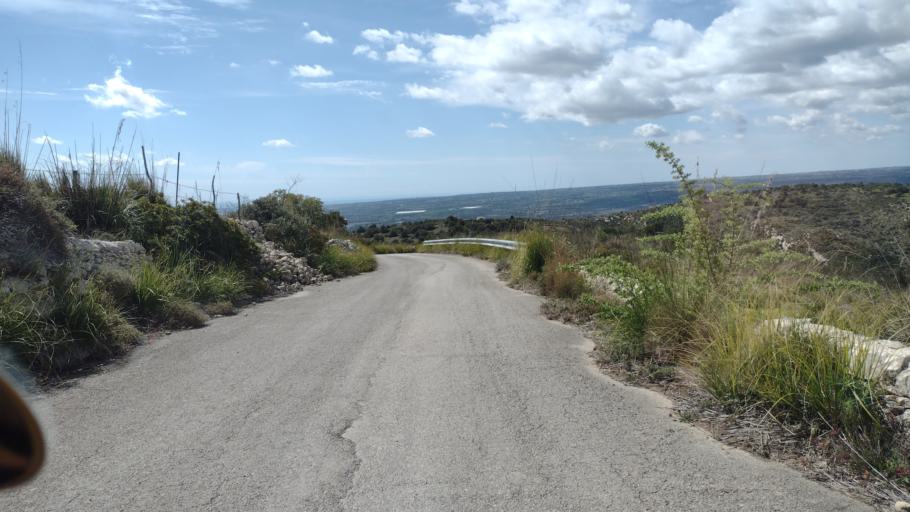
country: IT
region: Sicily
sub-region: Provincia di Siracusa
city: Rosolini
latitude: 36.9113
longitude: 14.9792
